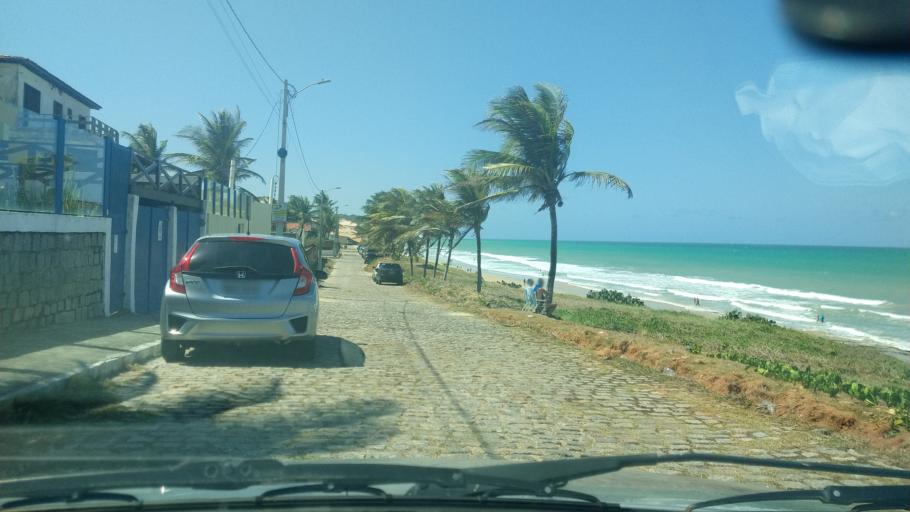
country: BR
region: Rio Grande do Norte
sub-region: Parnamirim
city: Parnamirim
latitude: -5.9493
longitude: -35.1533
